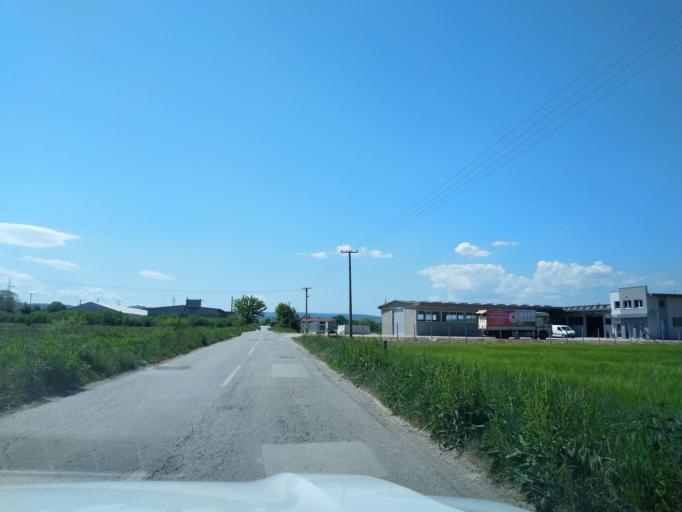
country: RS
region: Central Serbia
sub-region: Zlatiborski Okrug
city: Pozega
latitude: 43.8509
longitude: 20.0041
